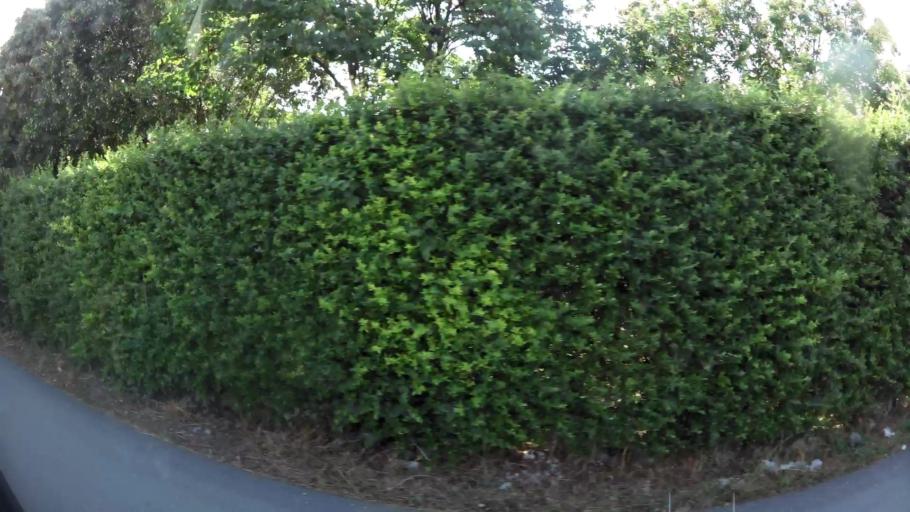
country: GR
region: Central Macedonia
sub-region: Nomos Pierias
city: Katerini
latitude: 40.2786
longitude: 22.4864
